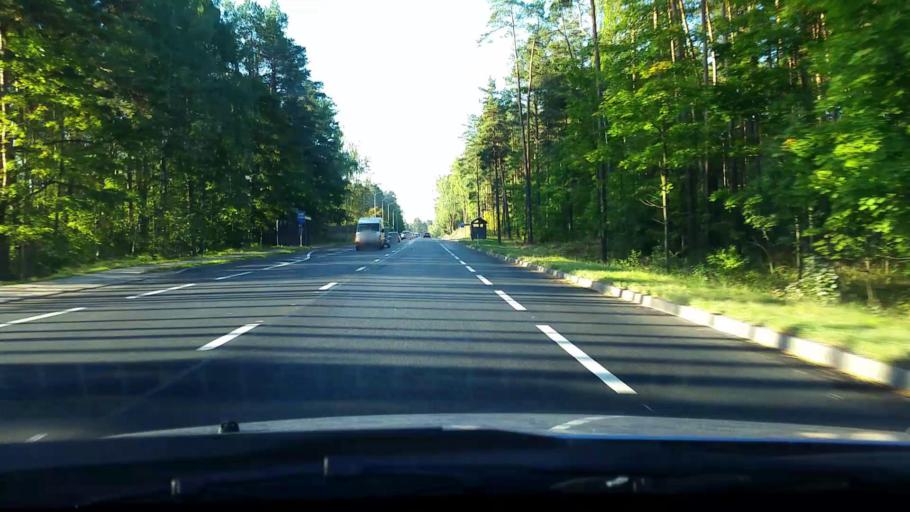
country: LV
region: Adazi
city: Adazi
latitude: 57.0487
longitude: 24.3176
